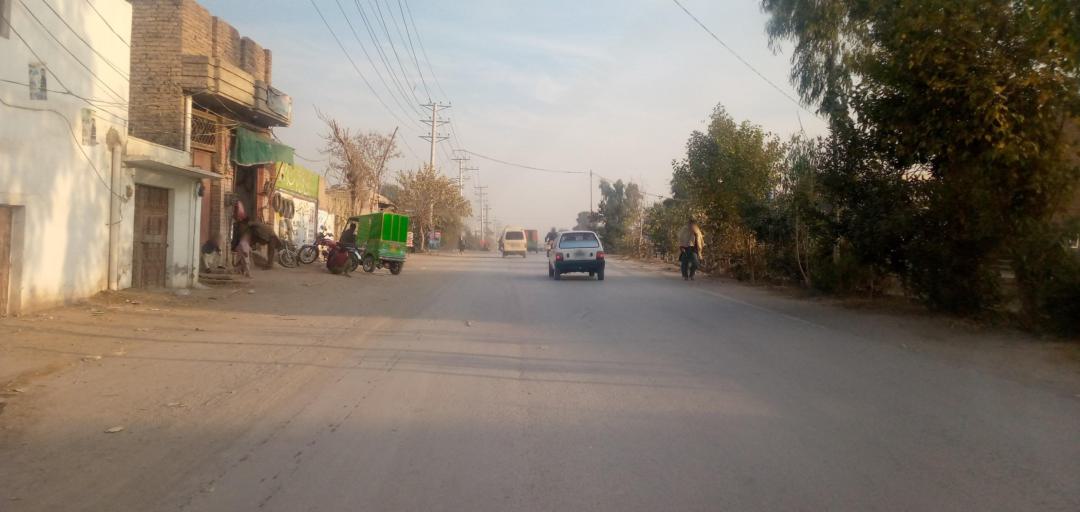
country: PK
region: Khyber Pakhtunkhwa
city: Peshawar
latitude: 33.9716
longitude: 71.5332
